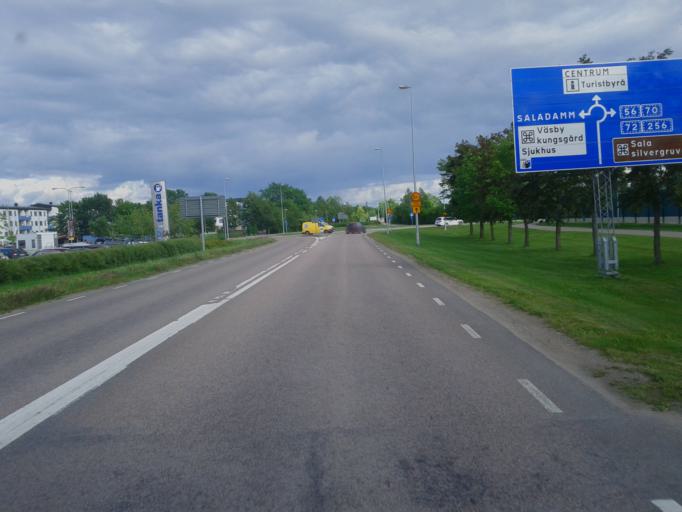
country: SE
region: Vaestmanland
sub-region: Sala Kommun
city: Sala
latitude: 59.9222
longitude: 16.5863
